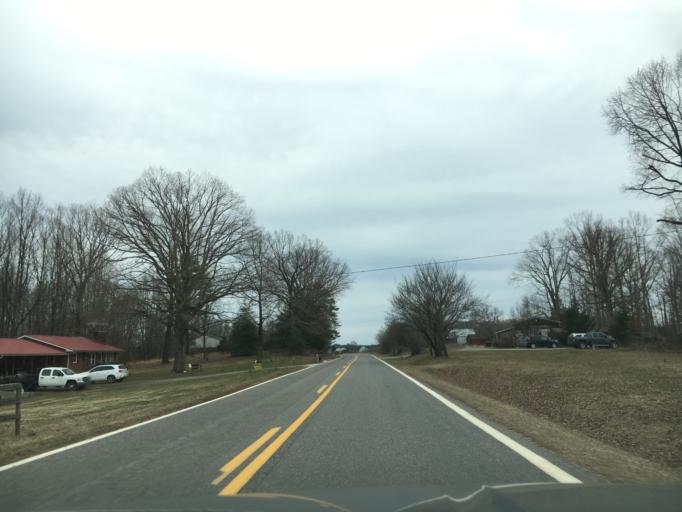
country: US
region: Virginia
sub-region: Charlotte County
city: Charlotte Court House
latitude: 37.0241
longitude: -78.7025
